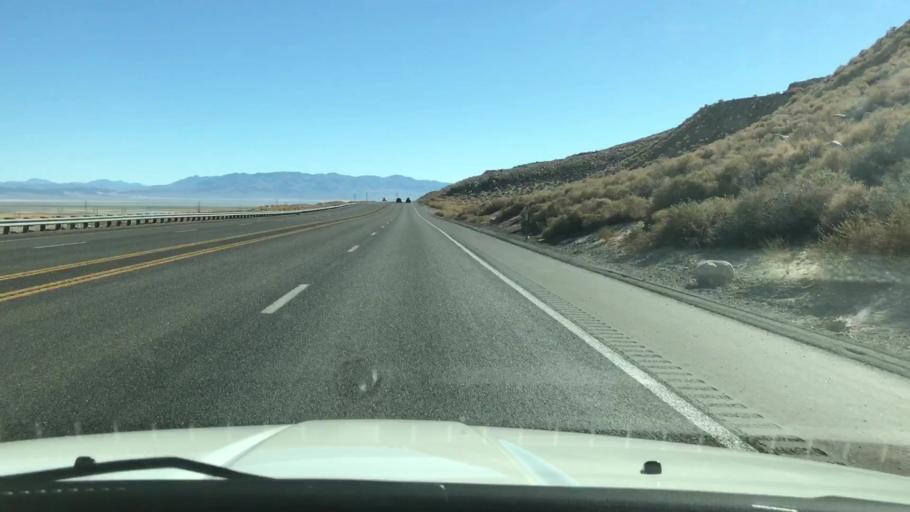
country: US
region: California
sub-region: Inyo County
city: Lone Pine
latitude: 36.5229
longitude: -118.0422
